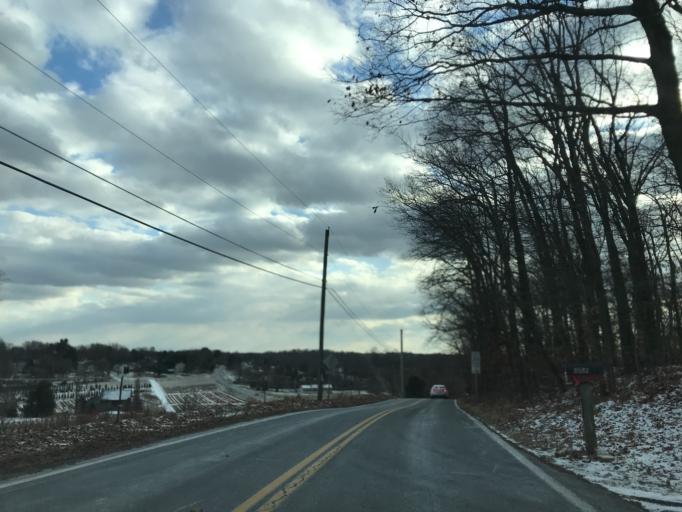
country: US
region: Maryland
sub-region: Harford County
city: Bel Air North
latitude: 39.6472
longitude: -76.3822
